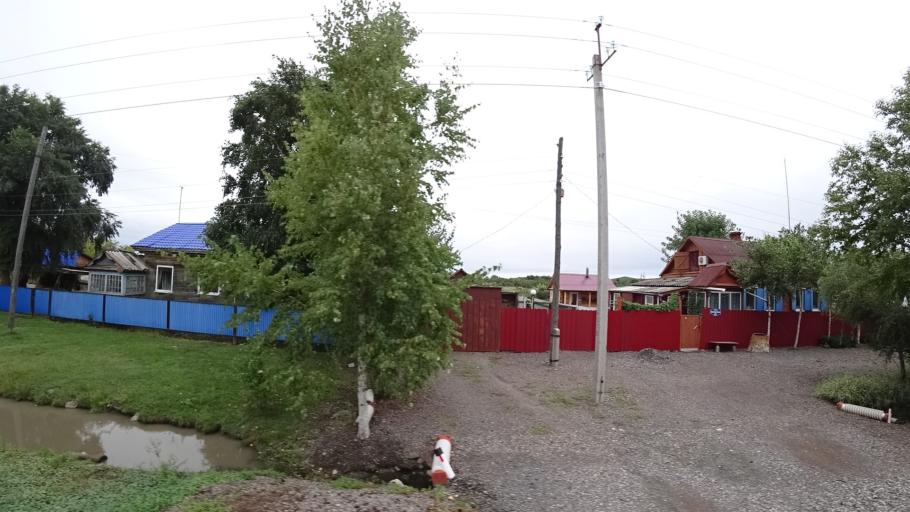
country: RU
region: Primorskiy
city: Chernigovka
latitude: 44.3358
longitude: 132.5951
